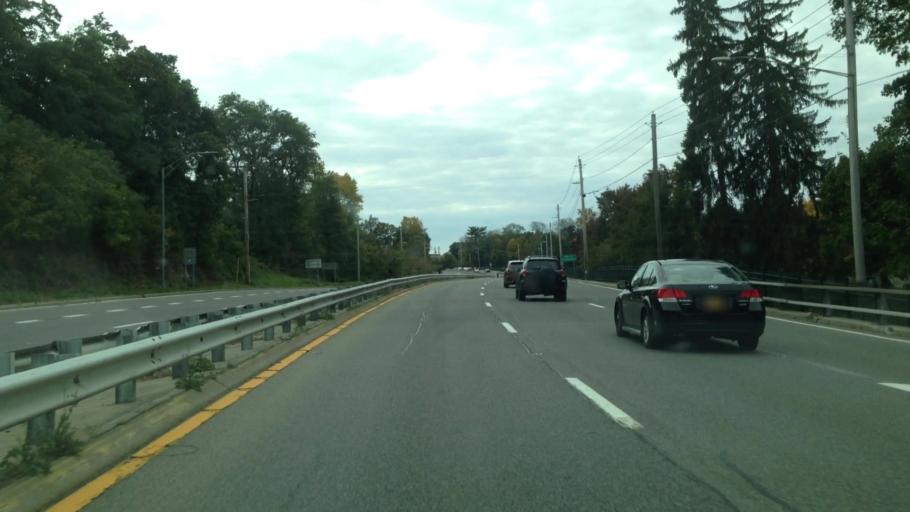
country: US
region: New York
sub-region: Dutchess County
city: Poughkeepsie
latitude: 41.6827
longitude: -73.9297
